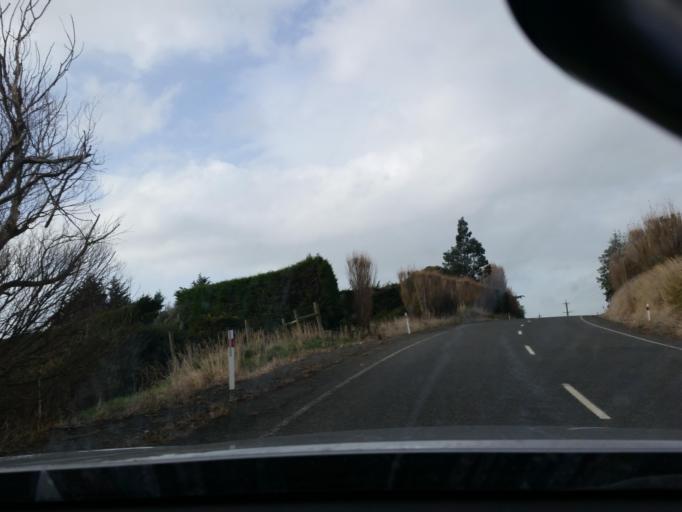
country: NZ
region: Southland
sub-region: Invercargill City
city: Invercargill
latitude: -46.3147
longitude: 168.3402
